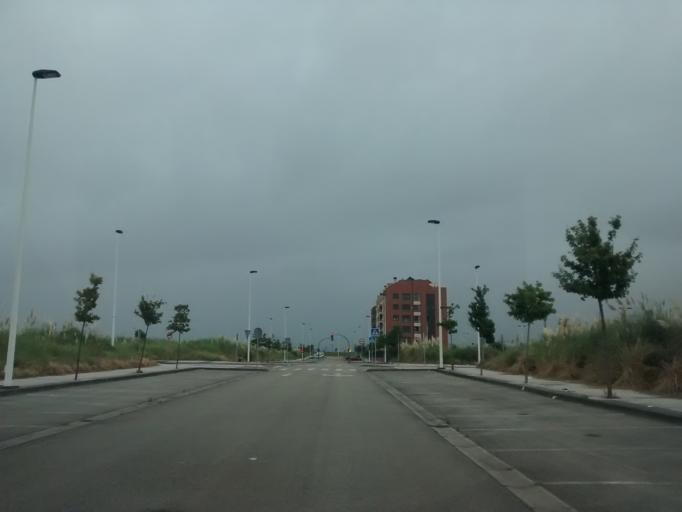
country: ES
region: Cantabria
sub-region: Provincia de Cantabria
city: Camargo
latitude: 43.4393
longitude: -3.8550
